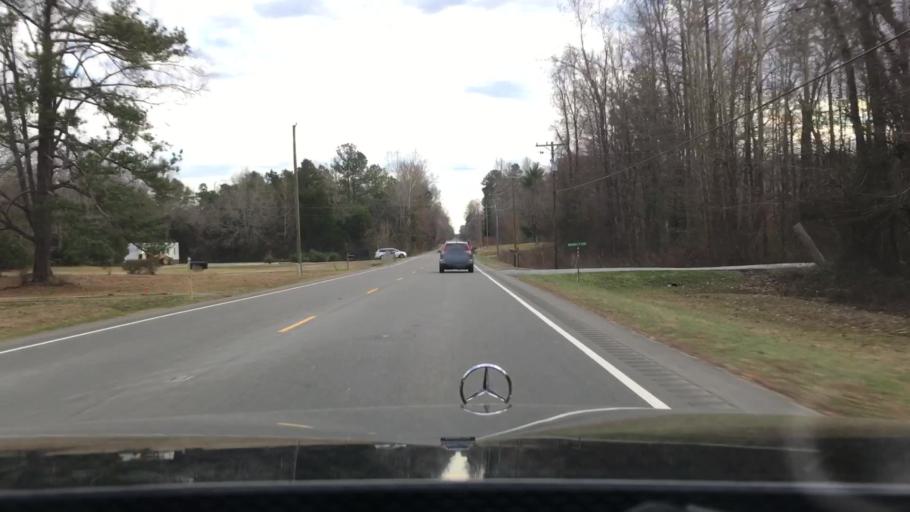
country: US
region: North Carolina
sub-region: Orange County
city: Hillsborough
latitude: 36.1223
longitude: -79.1154
